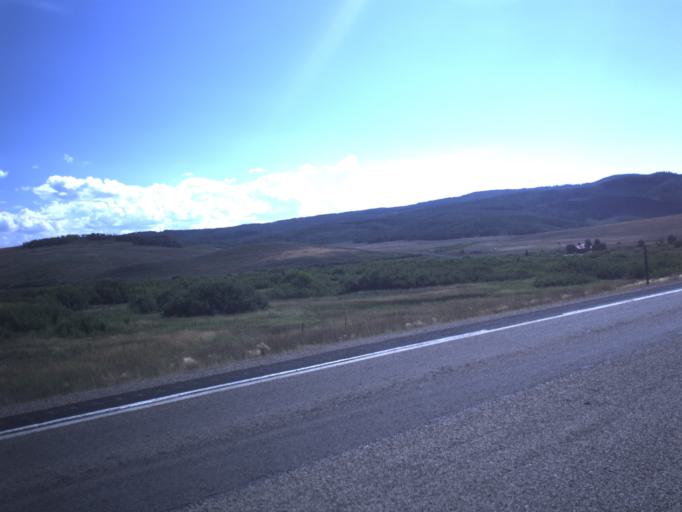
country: US
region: Utah
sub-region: Wasatch County
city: Heber
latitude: 40.2412
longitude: -111.1785
